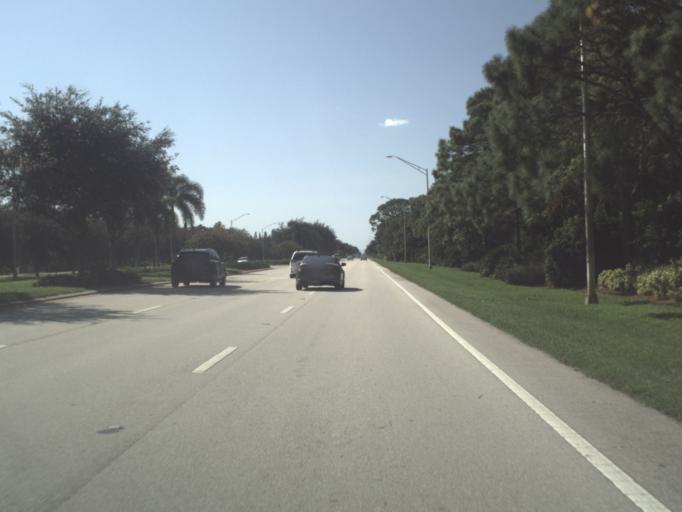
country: US
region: Florida
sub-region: Collier County
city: Pine Ridge
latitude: 26.2278
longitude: -81.8009
